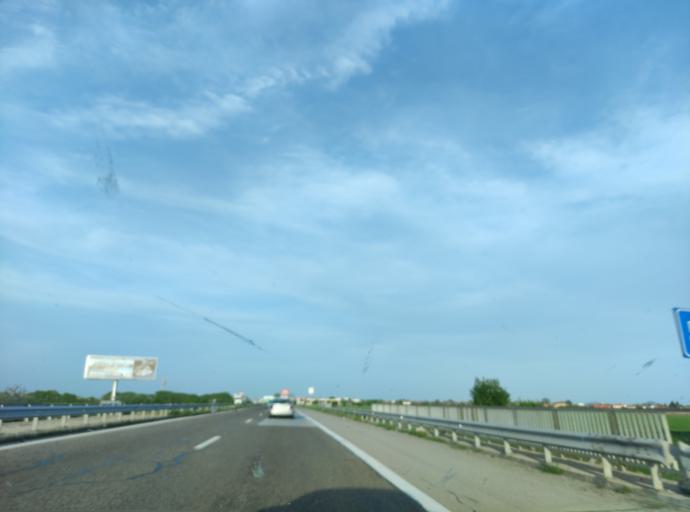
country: BG
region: Plovdiv
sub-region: Obshtina Suedinenie
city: Suedinenie
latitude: 42.1982
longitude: 24.6265
